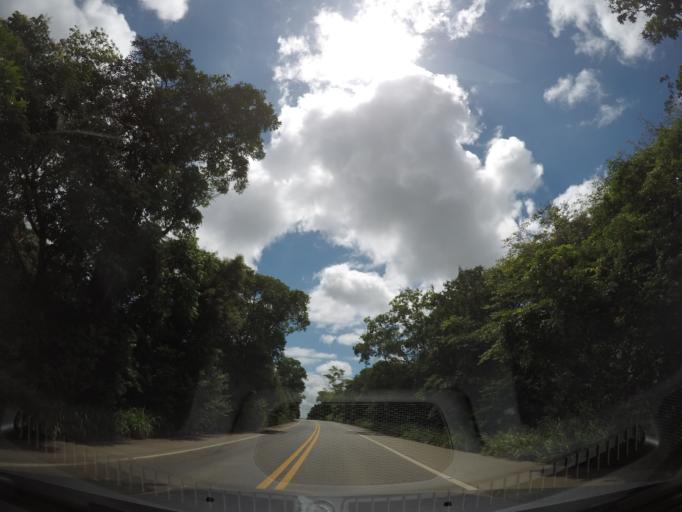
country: BR
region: Bahia
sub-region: Iraquara
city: Iraquara
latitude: -12.4817
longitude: -41.3548
